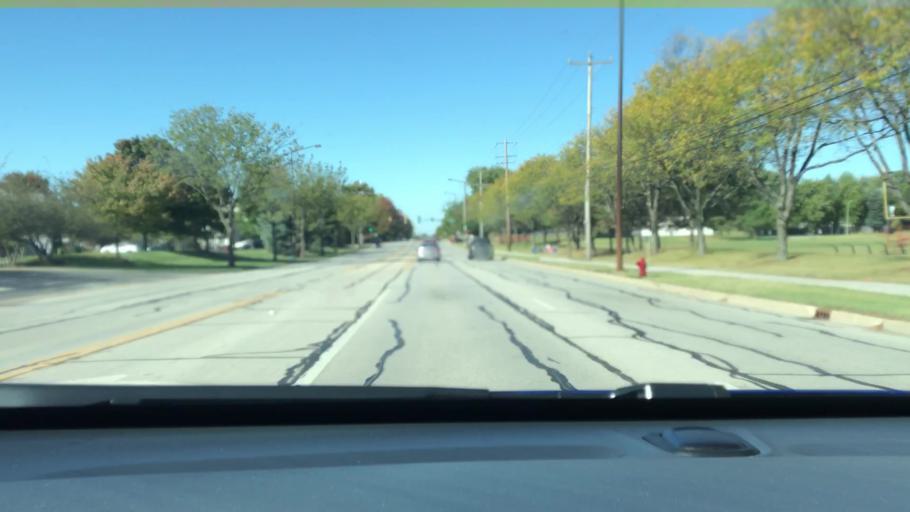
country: US
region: Illinois
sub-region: Kane County
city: North Aurora
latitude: 41.7811
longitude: -88.3567
